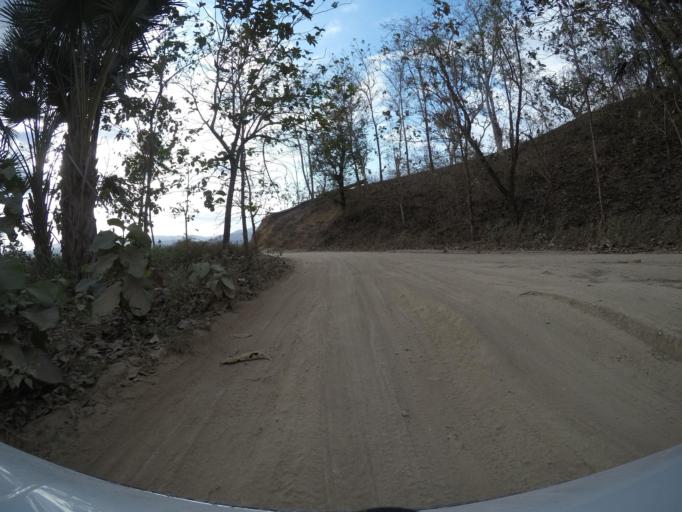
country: TL
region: Bobonaro
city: Maliana
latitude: -8.8872
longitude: 125.2087
